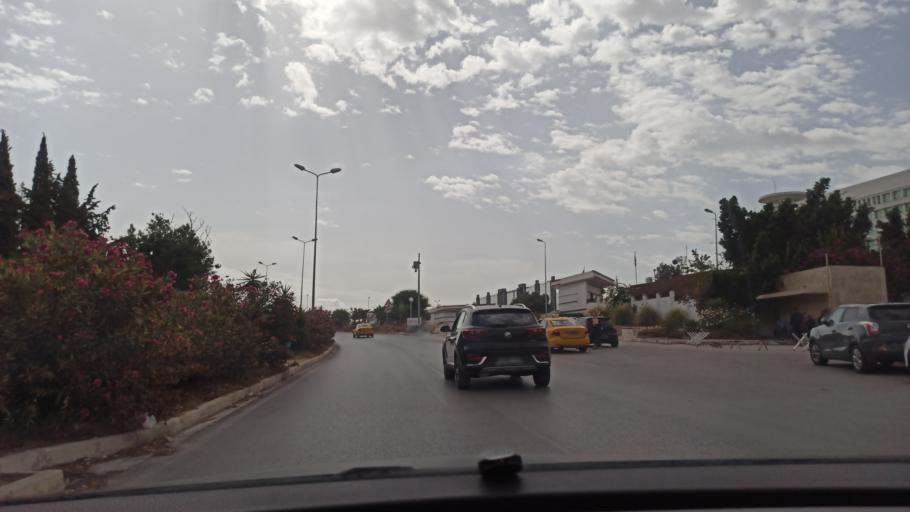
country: TN
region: Tunis
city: Tunis
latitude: 36.8302
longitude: 10.1583
